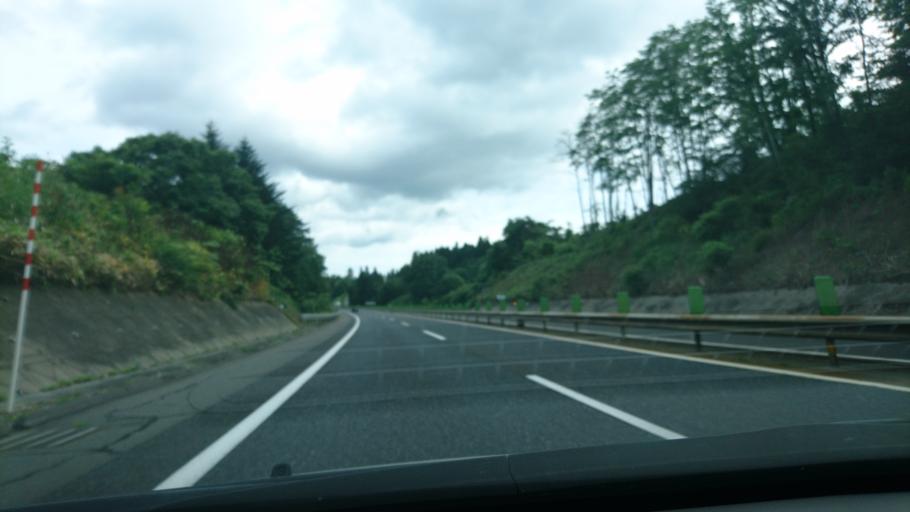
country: JP
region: Aomori
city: Hachinohe
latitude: 40.4216
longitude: 141.4394
